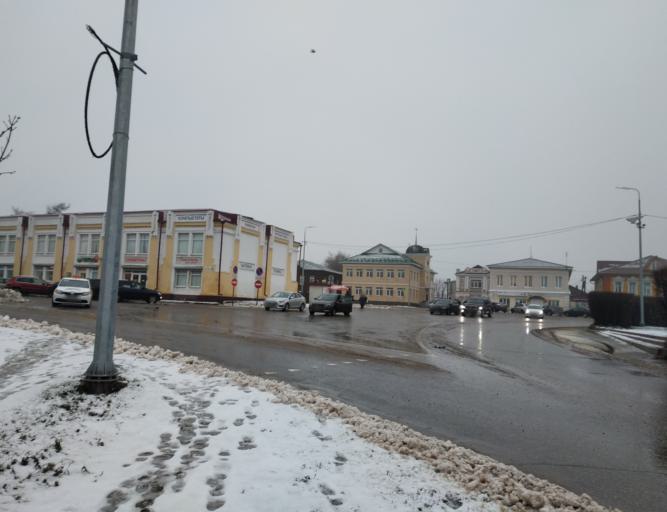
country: RU
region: Moskovskaya
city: Taldom
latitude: 56.7306
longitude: 37.5280
